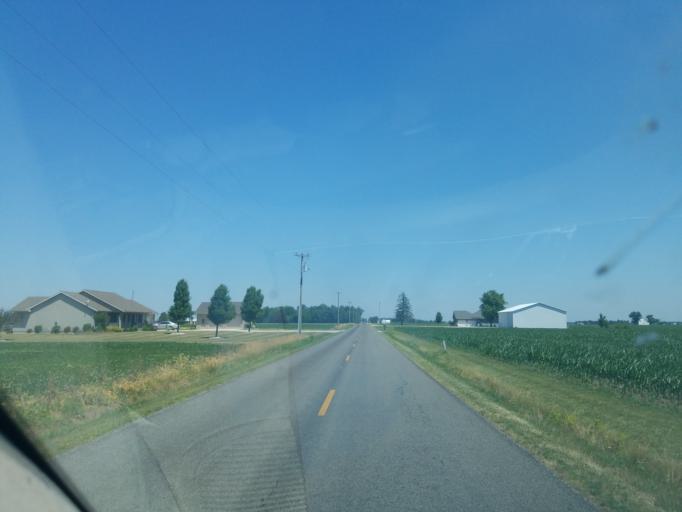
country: US
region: Ohio
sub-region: Mercer County
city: Rockford
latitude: 40.6483
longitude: -84.7086
